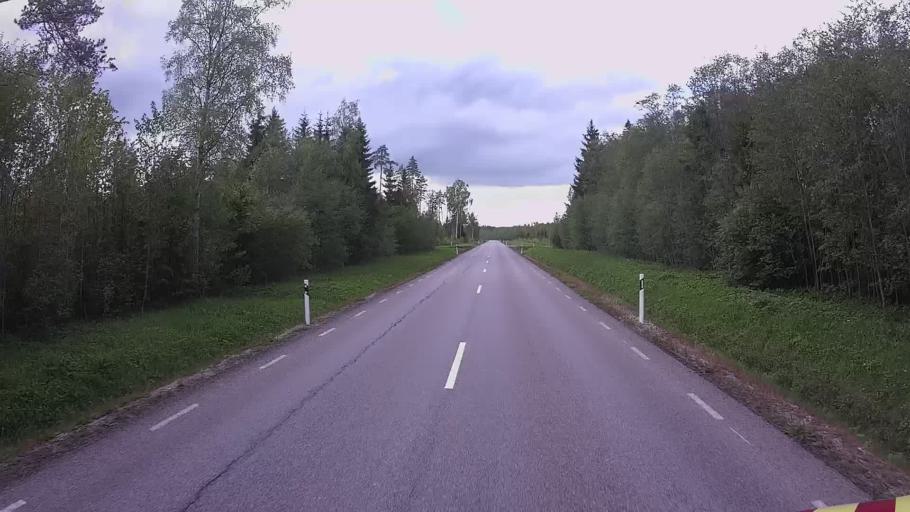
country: EE
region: Jogevamaa
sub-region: Mustvee linn
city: Mustvee
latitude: 59.0760
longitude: 26.9954
